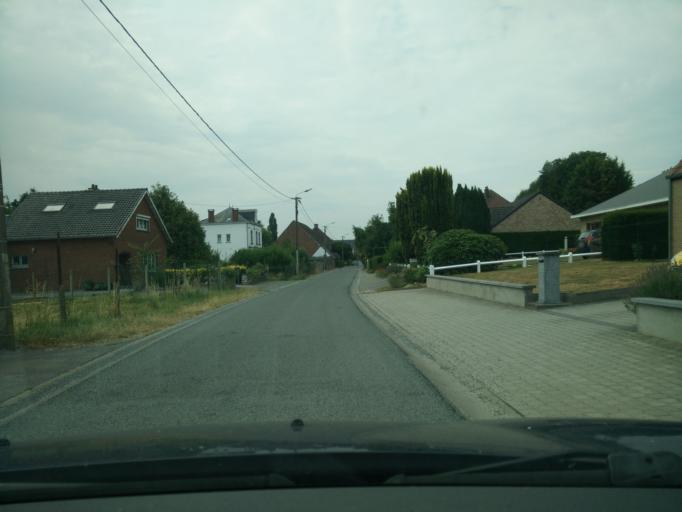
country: BE
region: Wallonia
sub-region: Province du Hainaut
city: Braine-le-Comte
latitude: 50.5924
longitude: 4.1364
